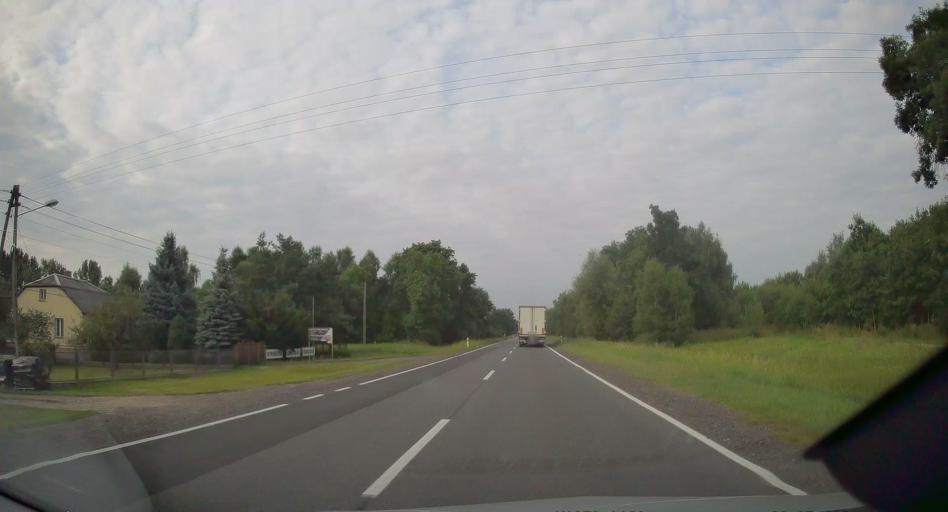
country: PL
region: Silesian Voivodeship
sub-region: Powiat czestochowski
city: Klomnice
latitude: 50.9322
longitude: 19.3815
